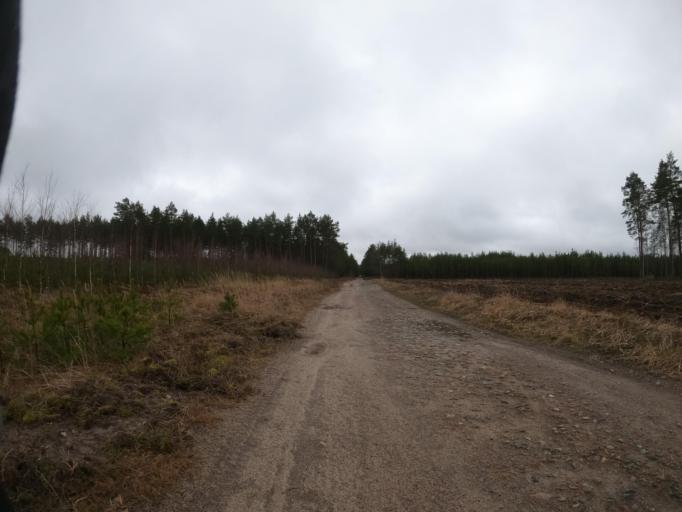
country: PL
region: Greater Poland Voivodeship
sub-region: Powiat zlotowski
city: Sypniewo
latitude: 53.5066
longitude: 16.5616
